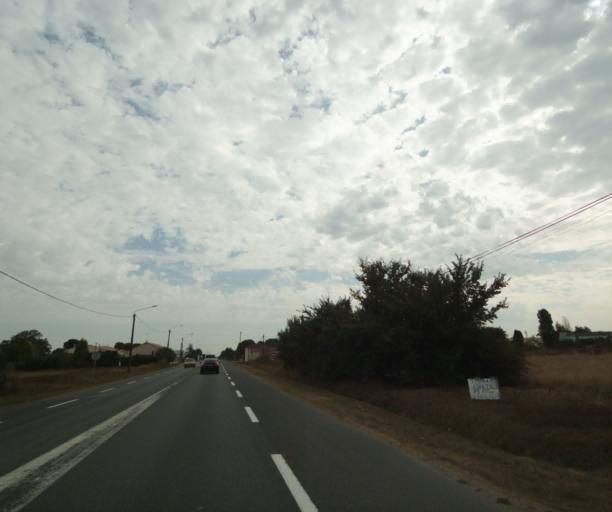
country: FR
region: Poitou-Charentes
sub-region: Departement de la Charente-Maritime
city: Tonnay-Charente
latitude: 45.9485
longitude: -0.9066
